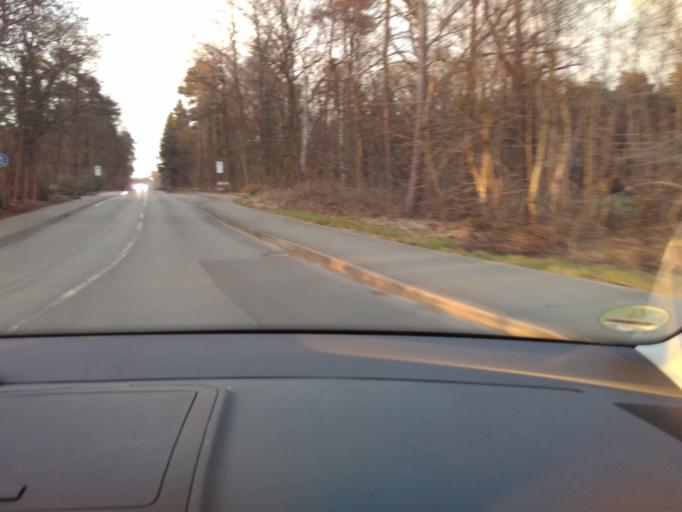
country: DE
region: North Rhine-Westphalia
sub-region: Regierungsbezirk Detmold
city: Verl
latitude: 51.9549
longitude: 8.5001
